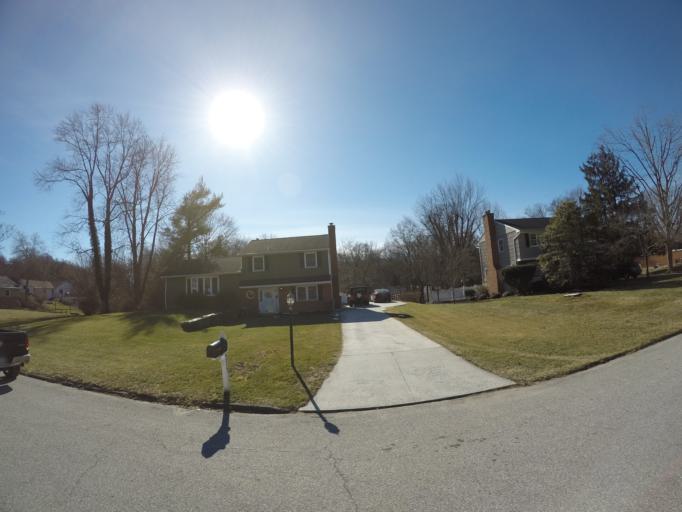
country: US
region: Maryland
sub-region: Howard County
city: Columbia
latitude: 39.2416
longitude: -76.8315
